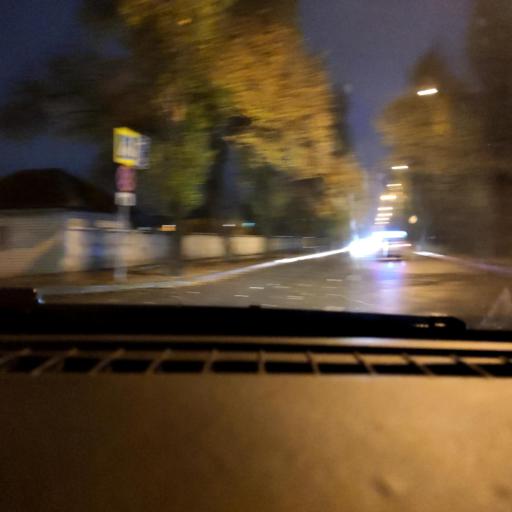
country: RU
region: Voronezj
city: Voronezh
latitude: 51.6828
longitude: 39.2557
